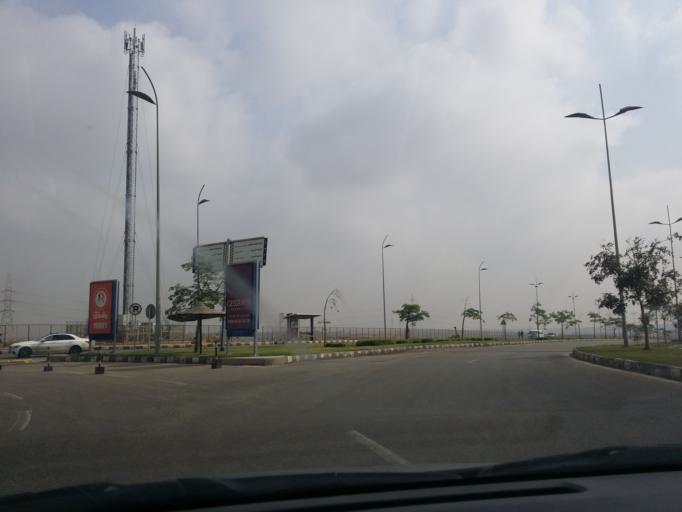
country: EG
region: Muhafazat al Qalyubiyah
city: Al Khankah
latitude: 30.1053
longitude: 31.6322
